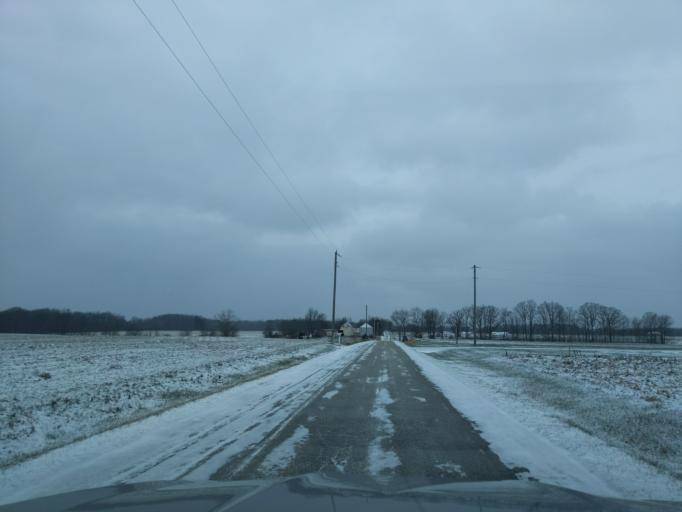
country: US
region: Indiana
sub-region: Decatur County
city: Greensburg
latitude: 39.2483
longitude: -85.4482
